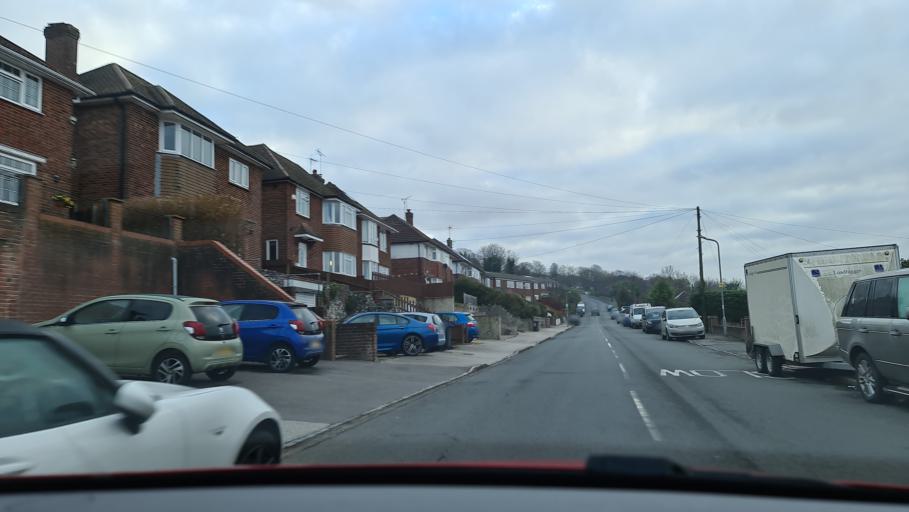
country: GB
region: England
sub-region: Buckinghamshire
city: High Wycombe
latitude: 51.6402
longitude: -0.7725
